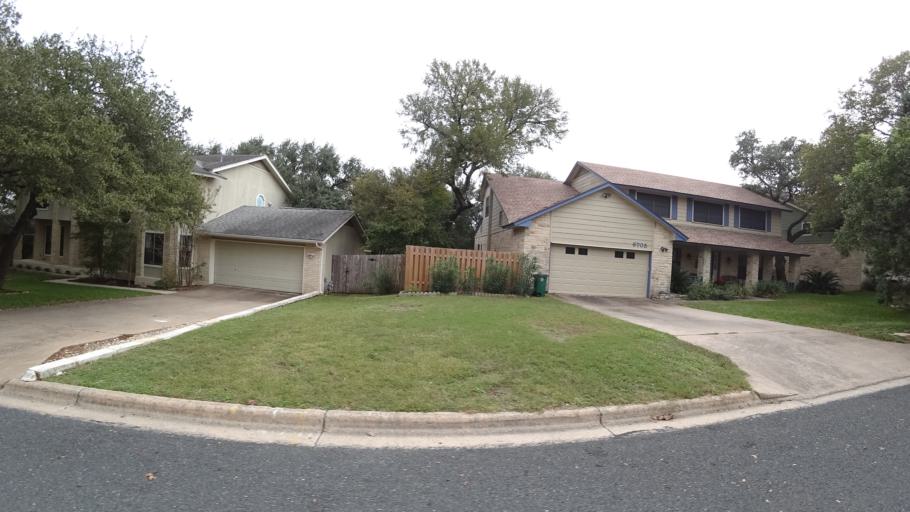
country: US
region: Texas
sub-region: Travis County
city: Barton Creek
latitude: 30.2291
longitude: -97.8746
